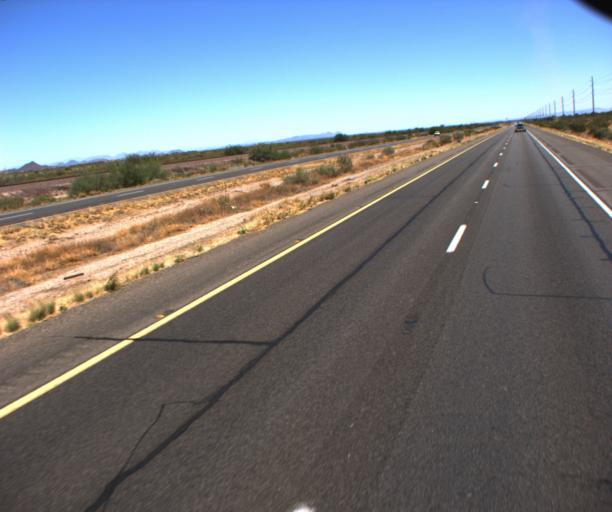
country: US
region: Arizona
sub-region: Maricopa County
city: Sun City West
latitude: 33.7302
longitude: -112.4678
